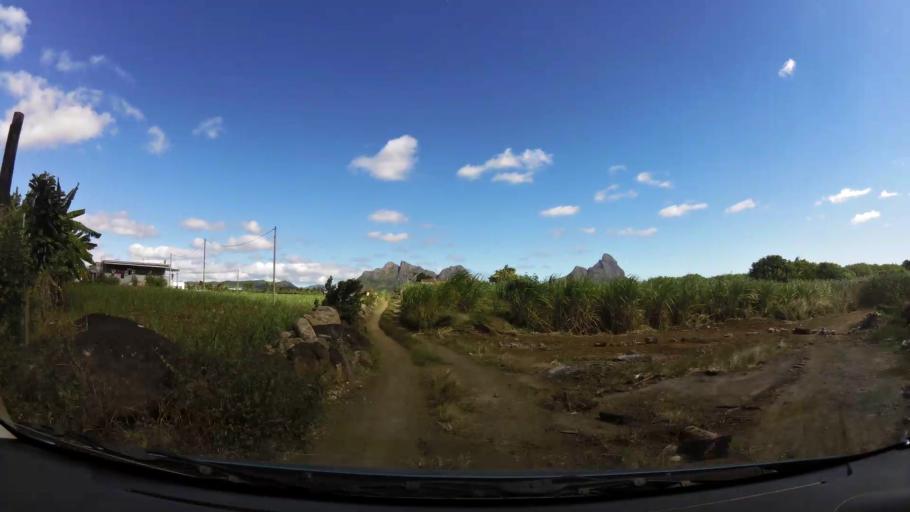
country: MU
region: Plaines Wilhems
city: Vacoas
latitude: -20.2823
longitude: 57.4718
